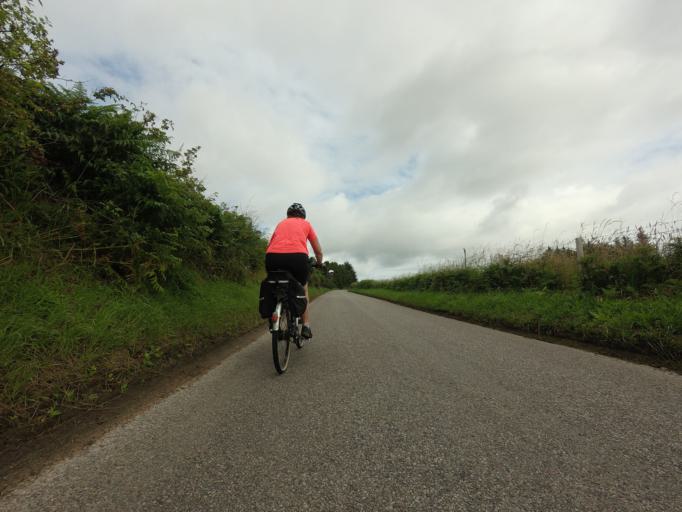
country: GB
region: Scotland
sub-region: Moray
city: Elgin
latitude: 57.6583
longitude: -3.3532
